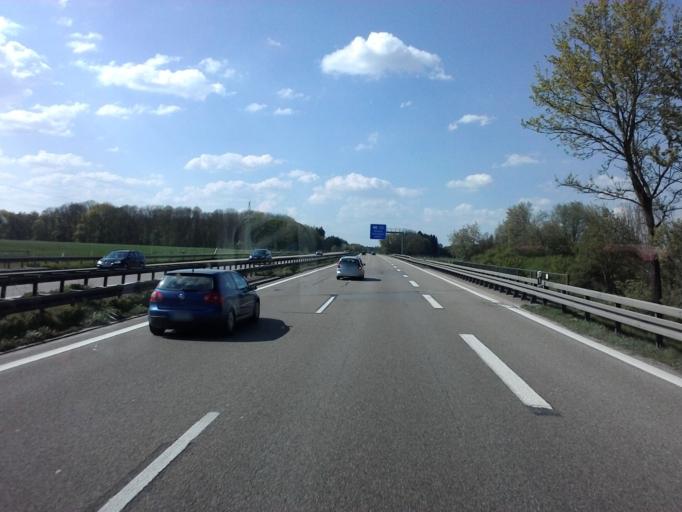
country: DE
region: Bavaria
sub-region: Swabia
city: Vohringen
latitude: 48.3021
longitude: 10.1063
